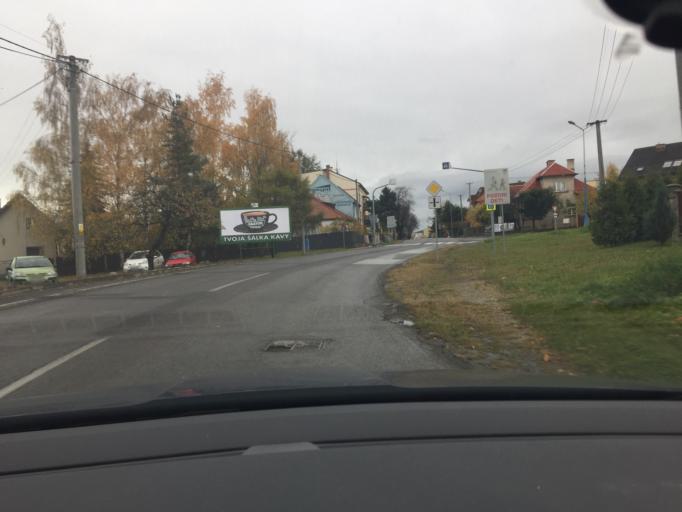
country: SK
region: Presovsky
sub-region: Okres Poprad
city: Poprad
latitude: 49.0652
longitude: 20.2842
